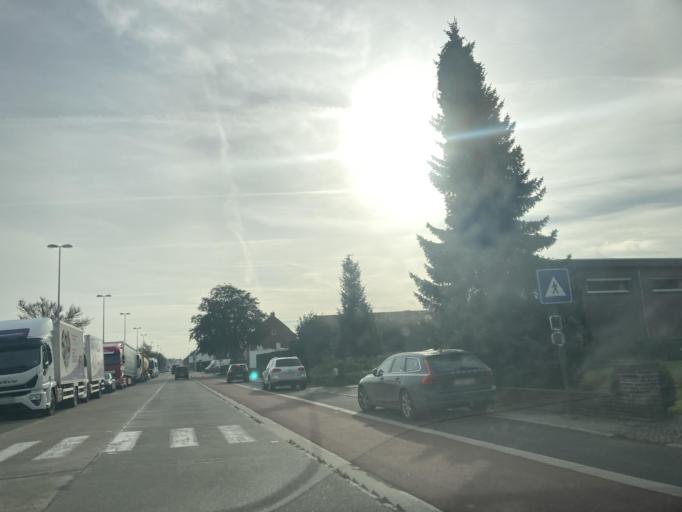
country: BE
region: Flanders
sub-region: Provincie West-Vlaanderen
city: Wervik
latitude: 50.7820
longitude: 3.0283
